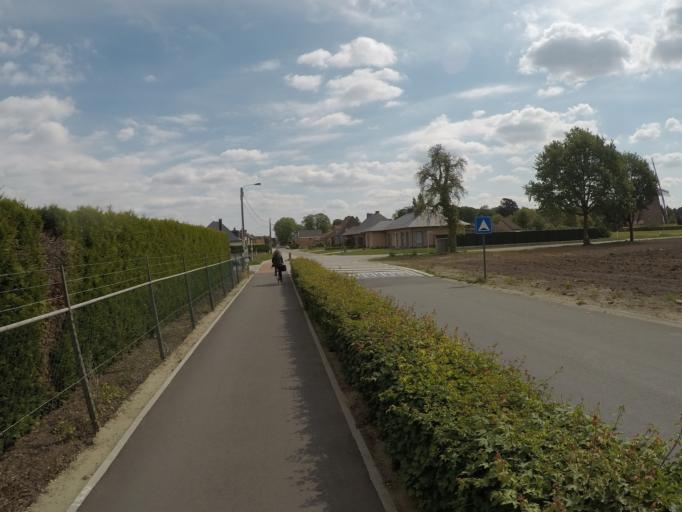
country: BE
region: Flanders
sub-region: Provincie Antwerpen
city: Zoersel
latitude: 51.2958
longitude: 4.6786
